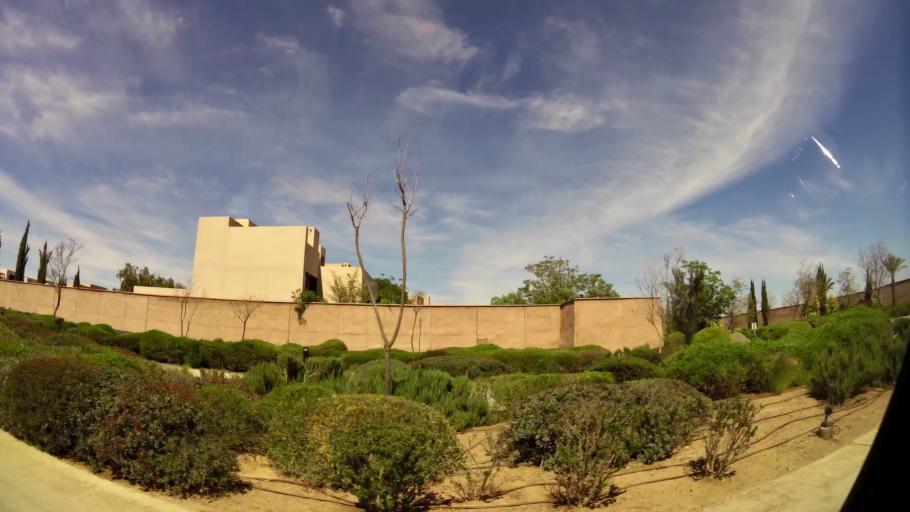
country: MA
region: Marrakech-Tensift-Al Haouz
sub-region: Marrakech
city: Marrakesh
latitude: 31.5999
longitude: -7.9491
